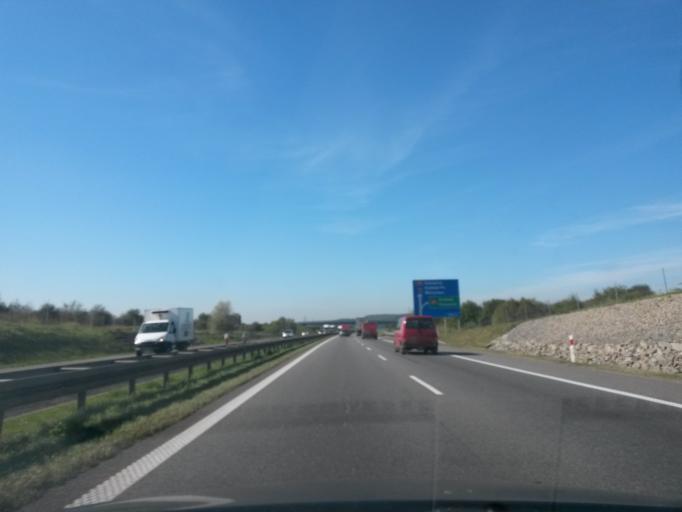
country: PL
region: Lesser Poland Voivodeship
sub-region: Krakow
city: Sidzina
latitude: 49.9916
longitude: 19.8803
